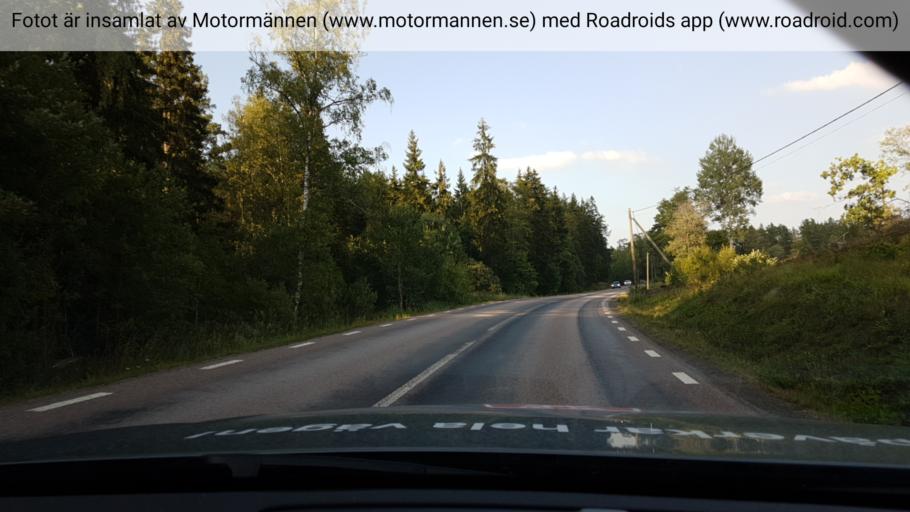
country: SE
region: Soedermanland
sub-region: Strangnas Kommun
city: Mariefred
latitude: 59.2302
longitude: 17.1687
